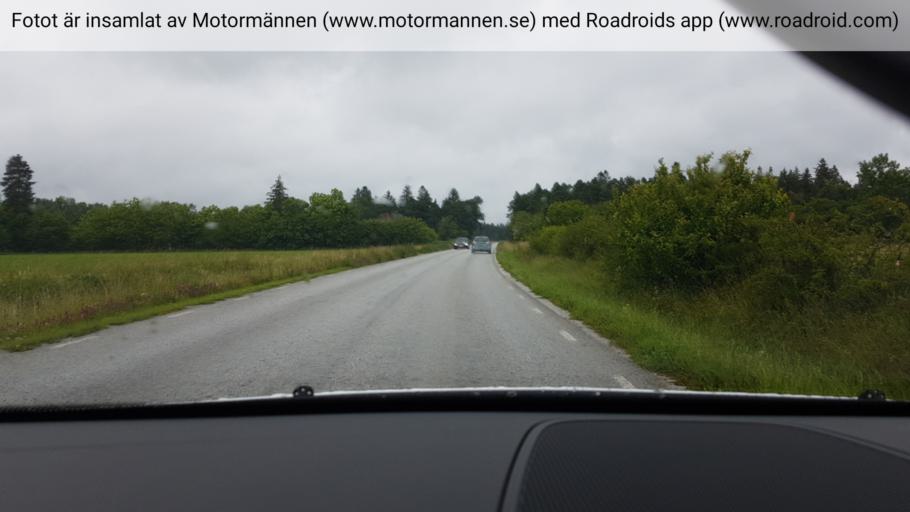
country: SE
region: Gotland
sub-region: Gotland
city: Slite
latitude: 57.5843
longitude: 18.7287
